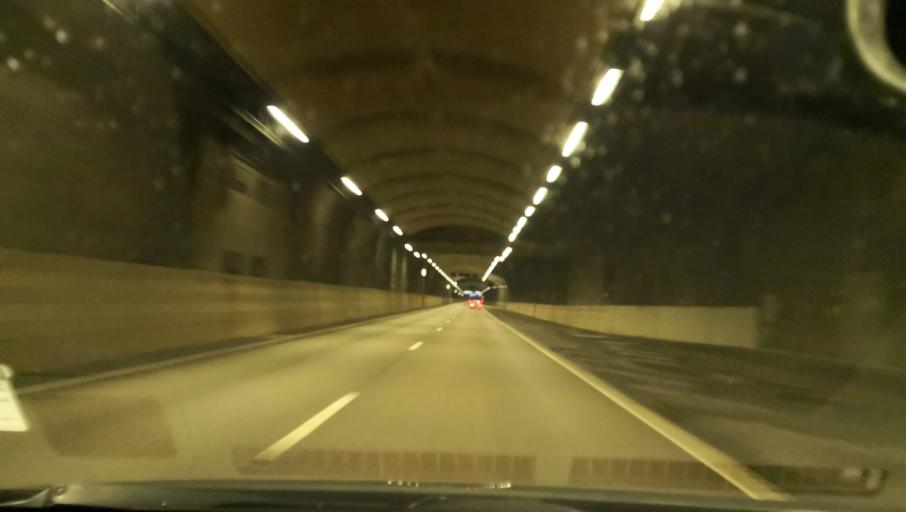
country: SE
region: Stockholm
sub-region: Stockholms Kommun
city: OEstermalm
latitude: 59.3001
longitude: 18.1027
